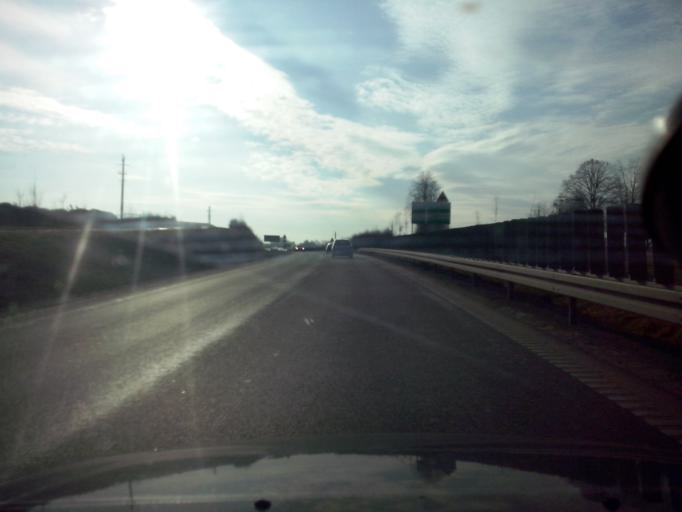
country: PL
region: Subcarpathian Voivodeship
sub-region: Powiat rzeszowski
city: Wolka Podlesna
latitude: 50.1539
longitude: 22.0778
